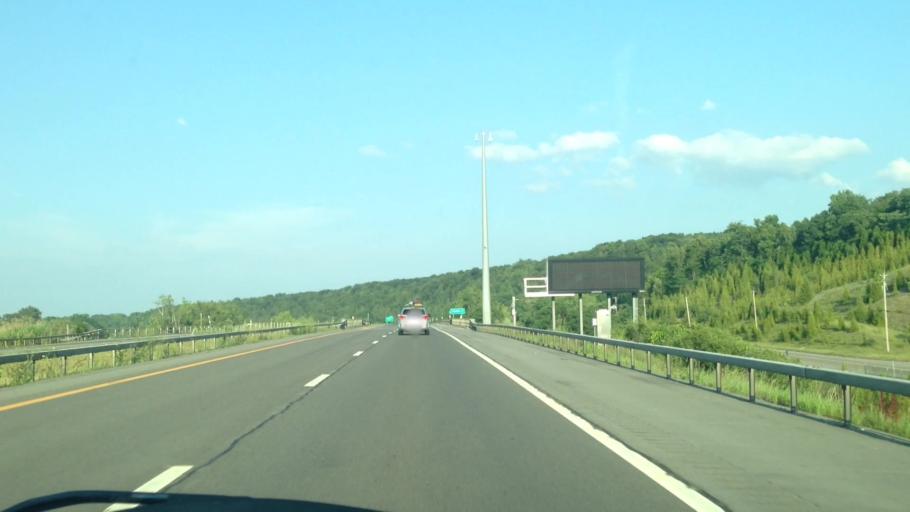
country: US
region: New York
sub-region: Onondaga County
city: Nedrow
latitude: 43.0042
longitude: -76.1055
